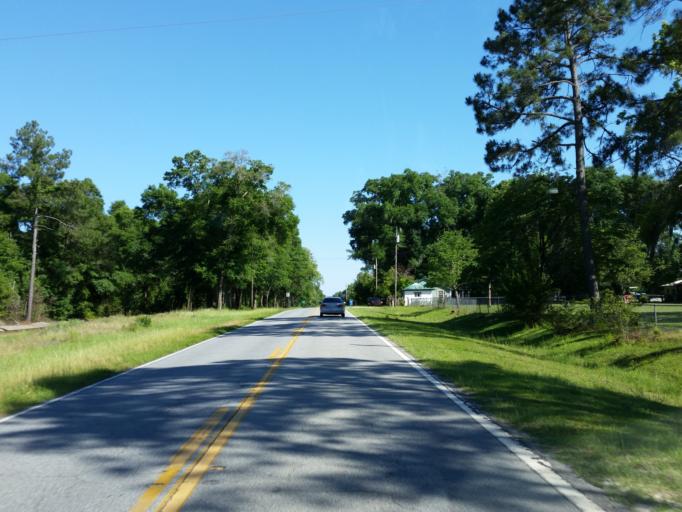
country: US
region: Georgia
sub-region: Echols County
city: Statenville
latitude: 30.6427
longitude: -83.1373
